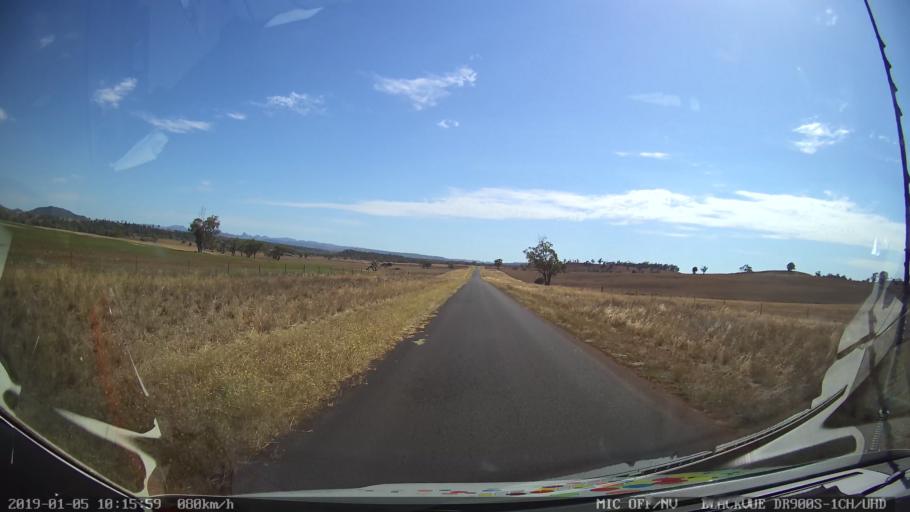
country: AU
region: New South Wales
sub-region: Gilgandra
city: Gilgandra
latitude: -31.5796
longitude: 148.9481
